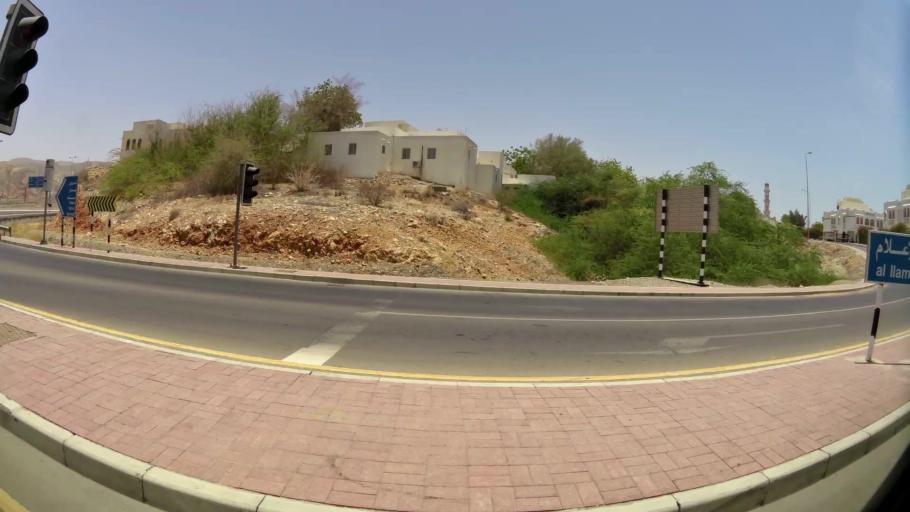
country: OM
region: Muhafazat Masqat
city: Muscat
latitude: 23.6064
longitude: 58.4891
